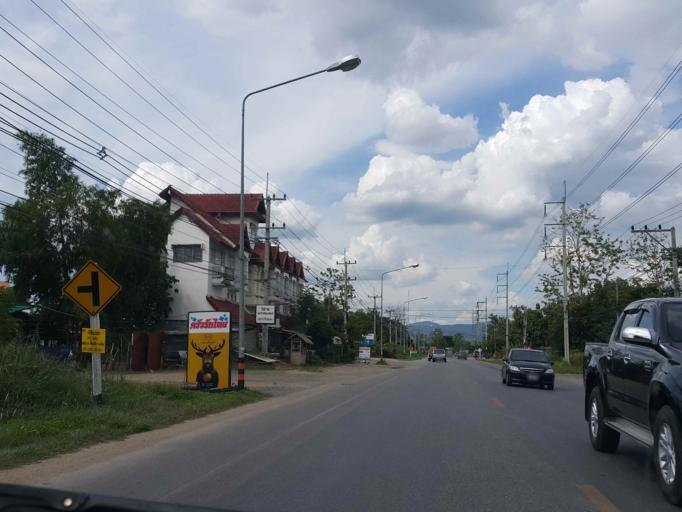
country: TH
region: Chiang Mai
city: San Sai
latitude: 18.9141
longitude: 98.9583
